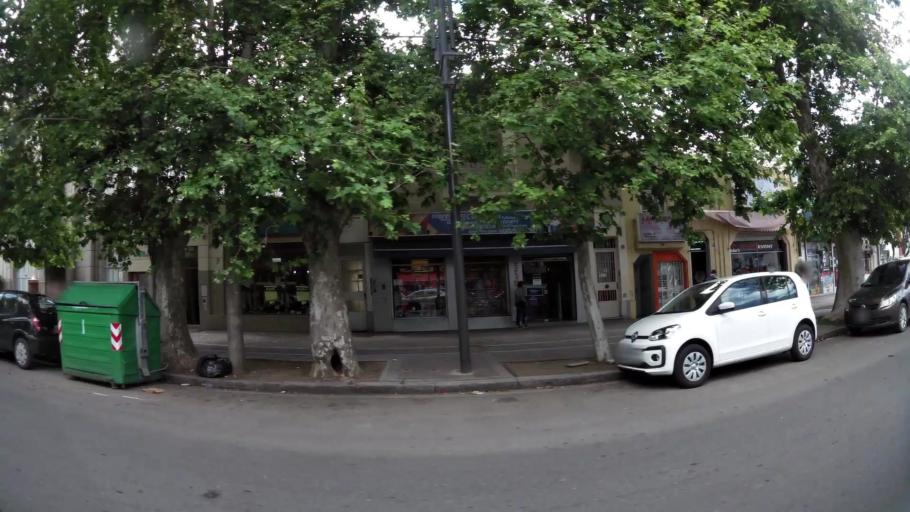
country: AR
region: Santa Fe
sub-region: Departamento de Rosario
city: Rosario
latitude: -32.9768
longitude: -60.6442
